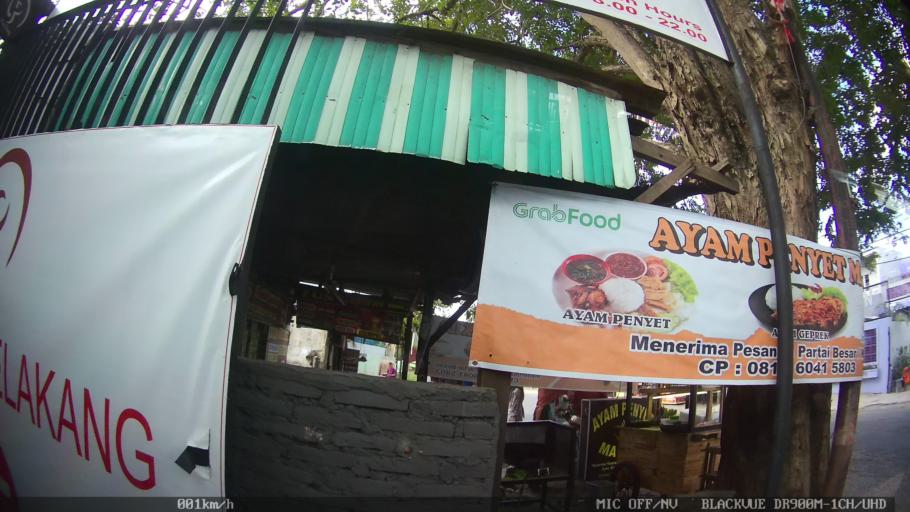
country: ID
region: North Sumatra
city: Medan
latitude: 3.6085
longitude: 98.6450
